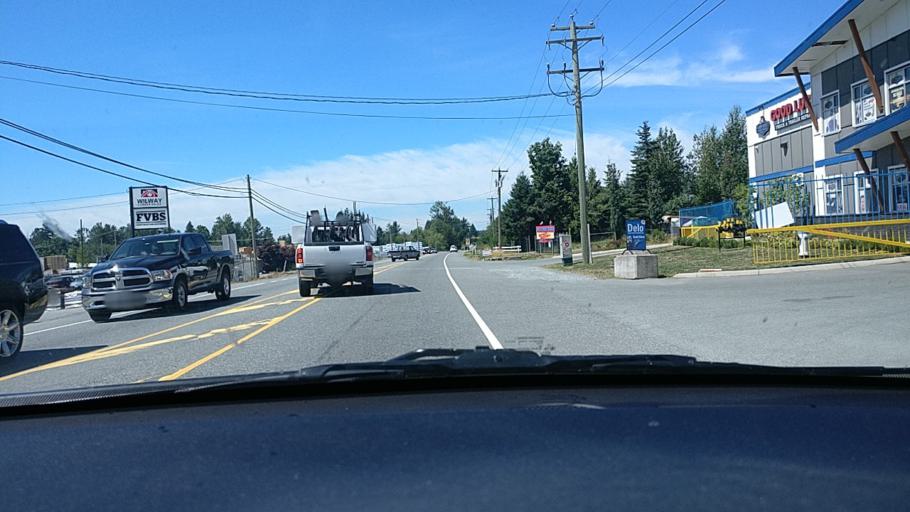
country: CA
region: British Columbia
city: Aldergrove
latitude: 49.0570
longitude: -122.4279
